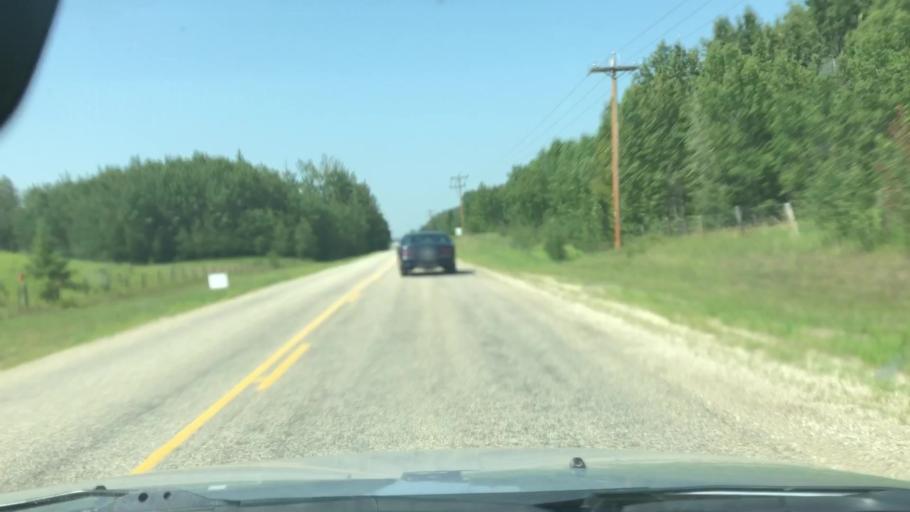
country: CA
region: Alberta
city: Devon
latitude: 53.4252
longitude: -113.7877
